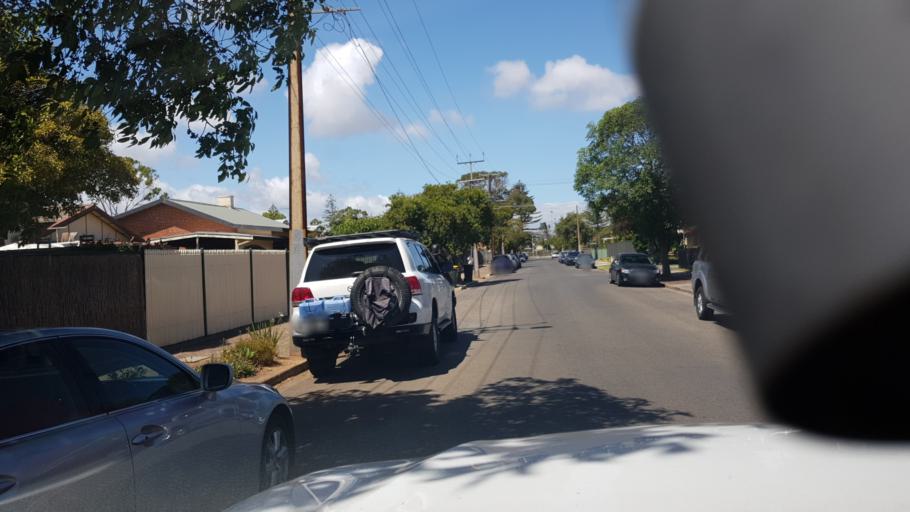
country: AU
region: South Australia
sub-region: Holdfast Bay
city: North Brighton
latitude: -35.0100
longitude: 138.5244
